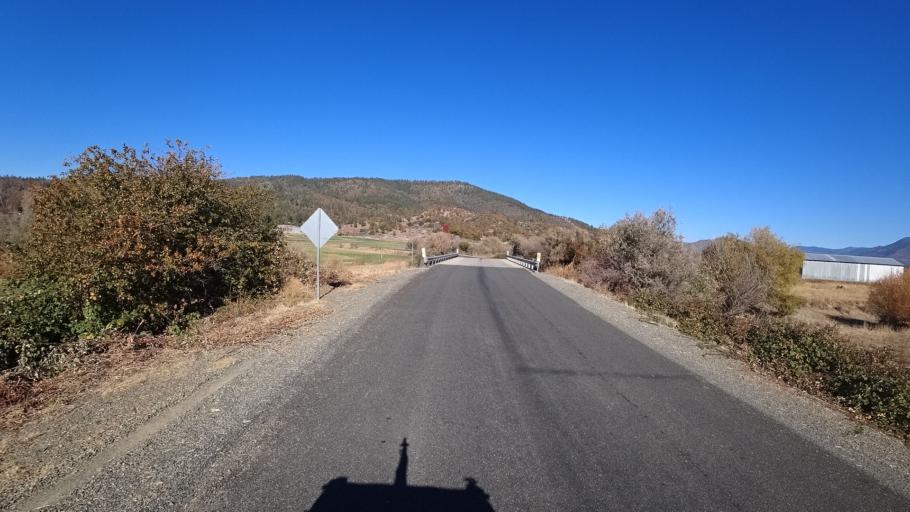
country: US
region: California
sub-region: Siskiyou County
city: Yreka
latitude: 41.5771
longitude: -122.8605
